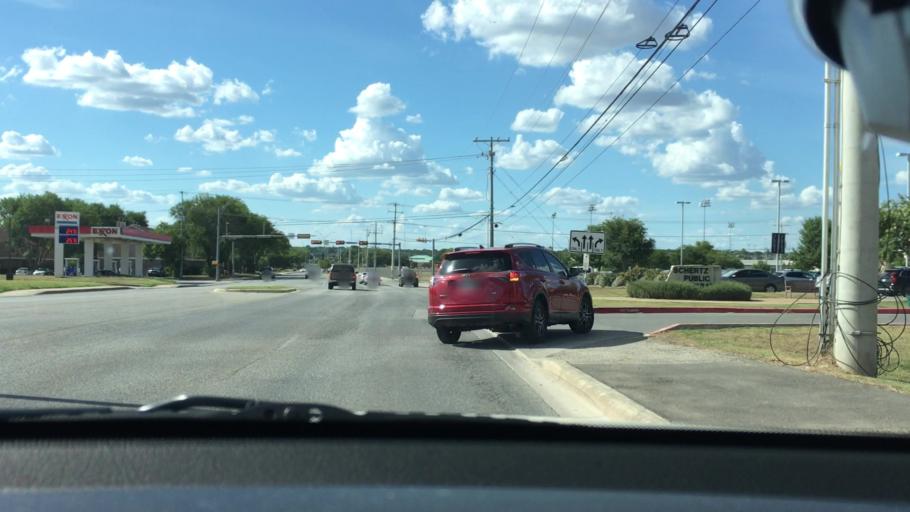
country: US
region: Texas
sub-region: Guadalupe County
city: Schertz
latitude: 29.5600
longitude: -98.2668
